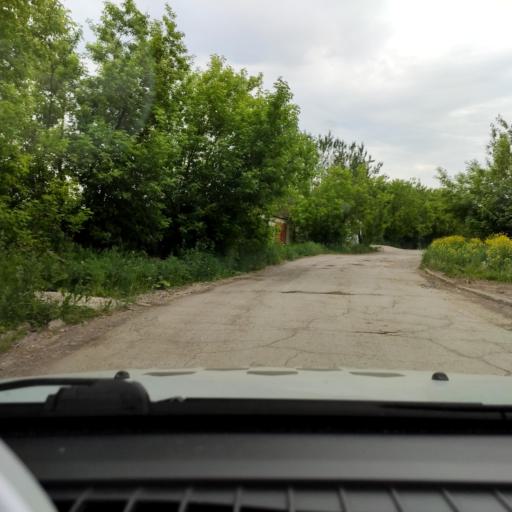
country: RU
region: Perm
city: Perm
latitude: 57.9749
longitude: 56.2879
